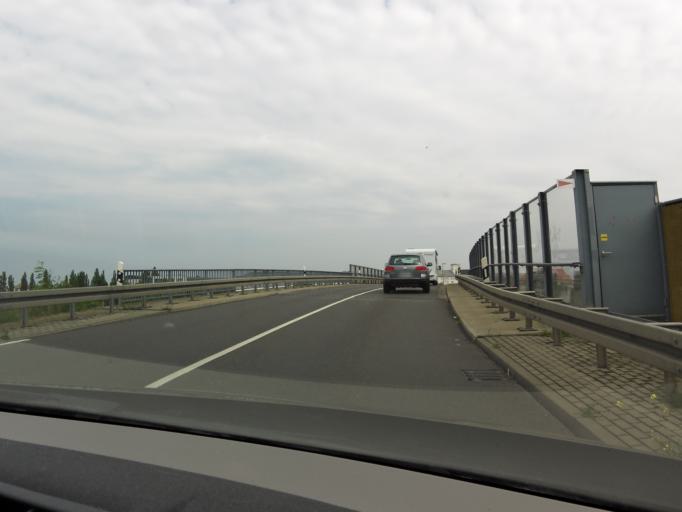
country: DE
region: Saxony-Anhalt
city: Wittenburg
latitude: 51.8648
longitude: 12.6334
